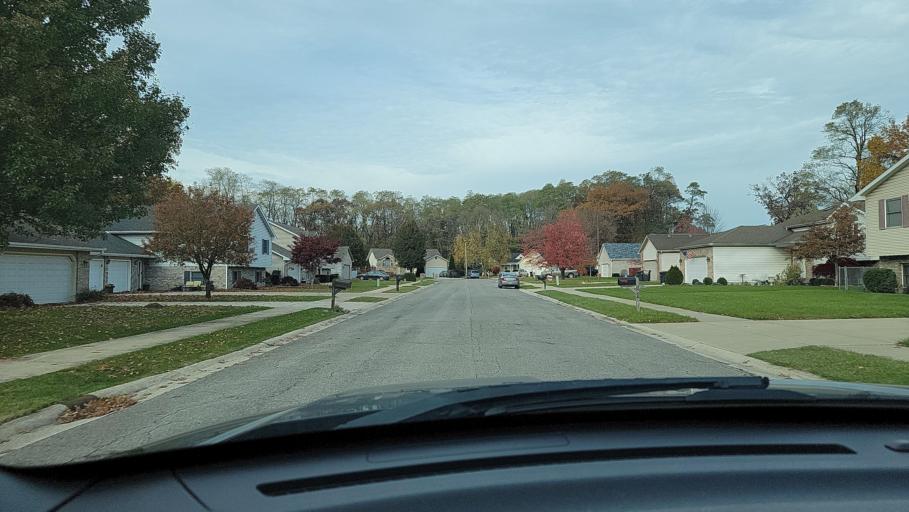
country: US
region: Indiana
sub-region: Porter County
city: Portage
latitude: 41.5963
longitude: -87.1593
